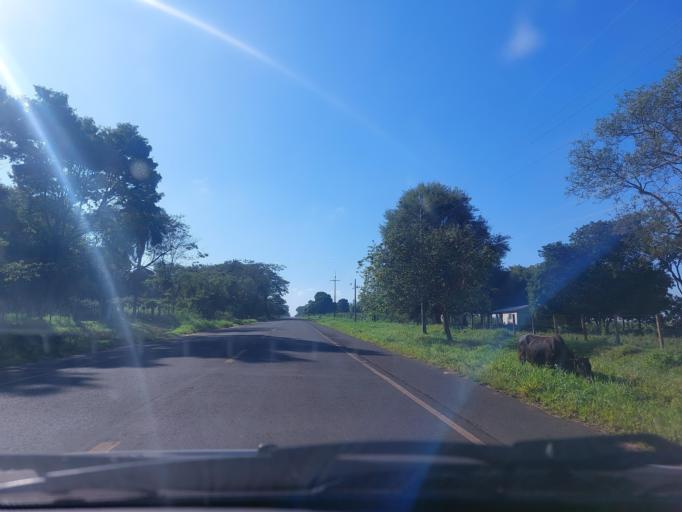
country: PY
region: San Pedro
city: Guayaybi
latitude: -24.5320
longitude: -56.5064
